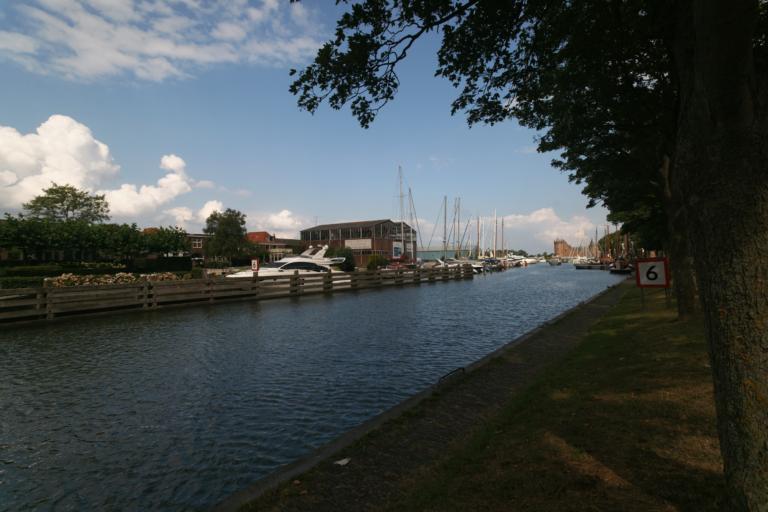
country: NL
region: North Holland
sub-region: Gemeente Weesp
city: Weesp
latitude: 52.3306
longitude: 5.0698
